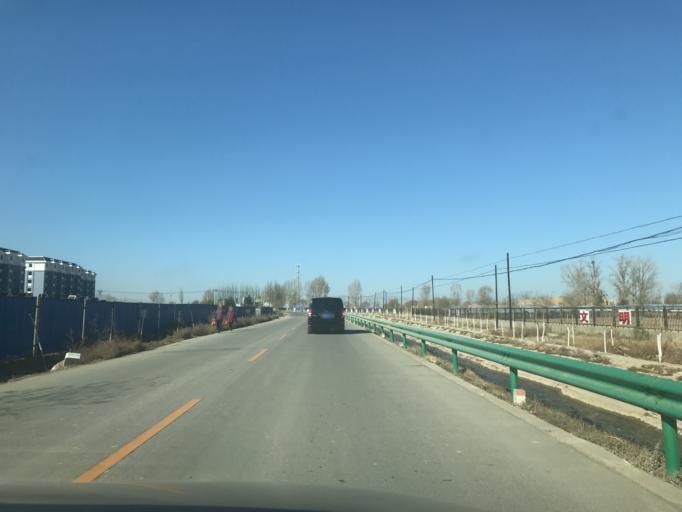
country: CN
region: Gansu Sheng
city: Gulang
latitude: 37.6764
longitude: 102.8389
